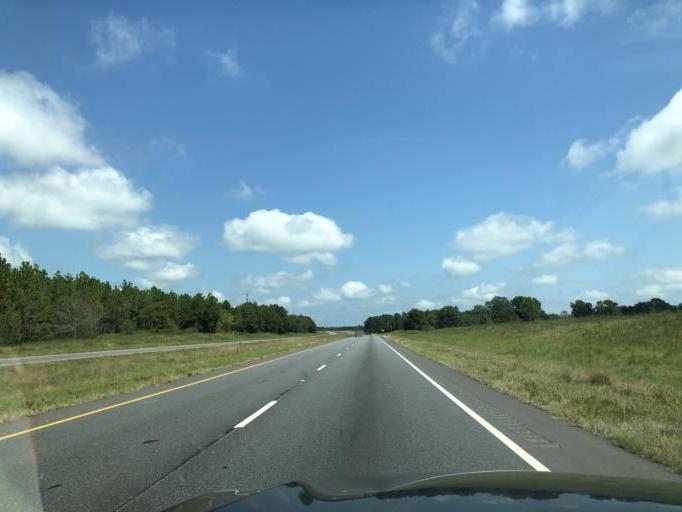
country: US
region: Alabama
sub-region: Henry County
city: Abbeville
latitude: 31.4970
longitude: -85.2941
